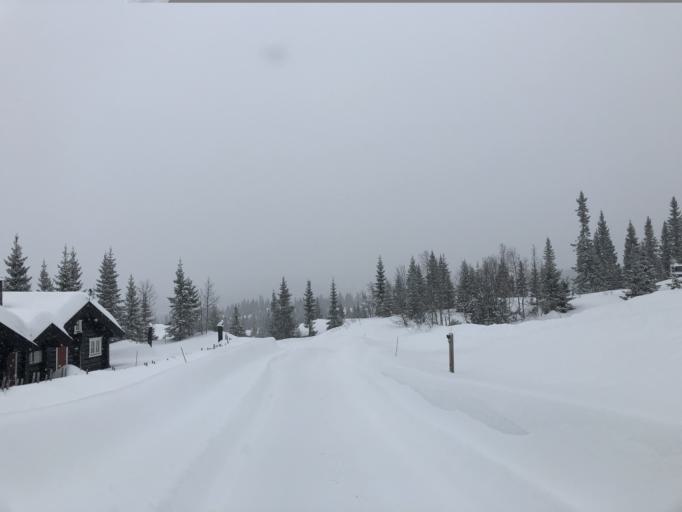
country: NO
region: Oppland
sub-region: Gausdal
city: Segalstad bru
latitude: 61.3282
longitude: 10.0536
